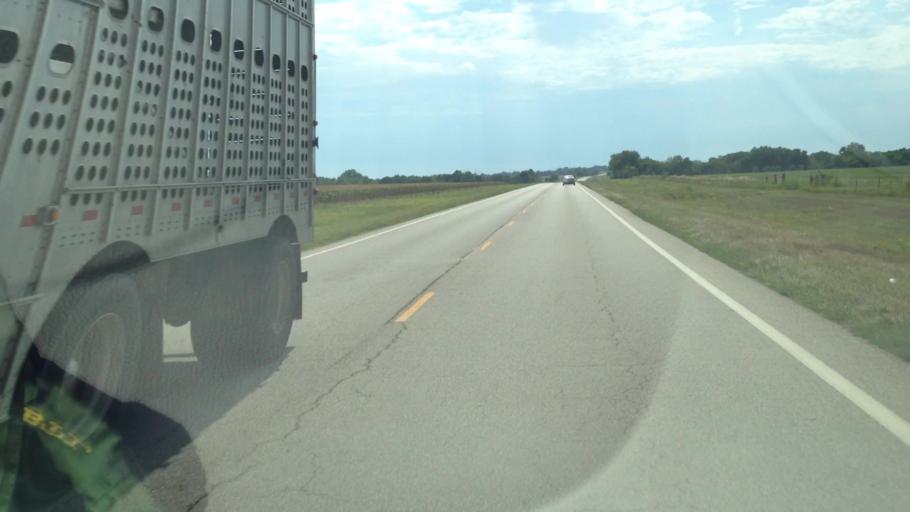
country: US
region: Kansas
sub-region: Labette County
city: Altamont
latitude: 37.1934
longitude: -95.2162
